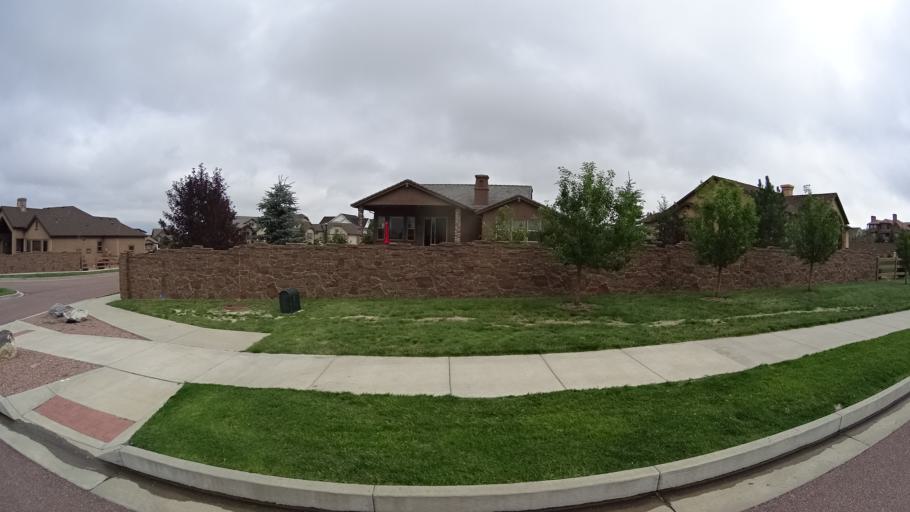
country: US
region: Colorado
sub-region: El Paso County
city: Gleneagle
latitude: 39.0281
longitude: -104.7903
